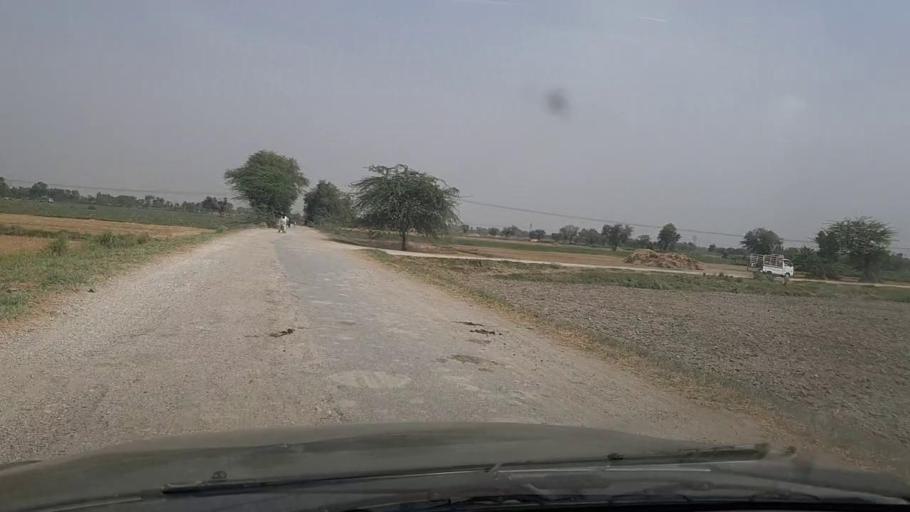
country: PK
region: Sindh
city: Shikarpur
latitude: 27.9218
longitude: 68.6749
